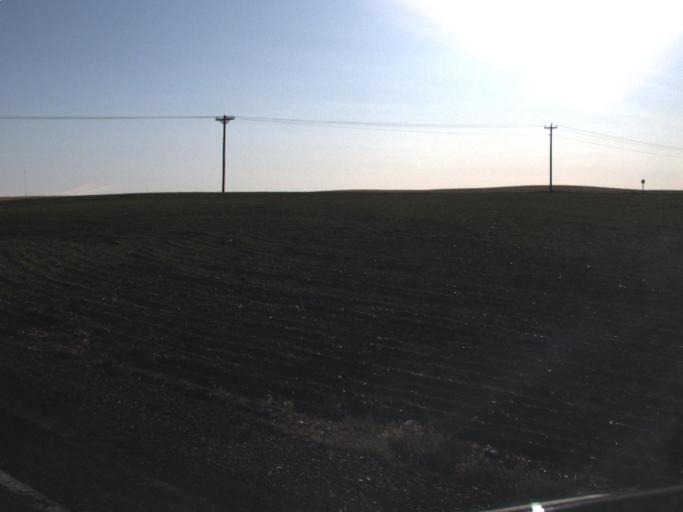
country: US
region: Washington
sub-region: Adams County
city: Ritzville
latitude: 46.8693
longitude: -118.3357
